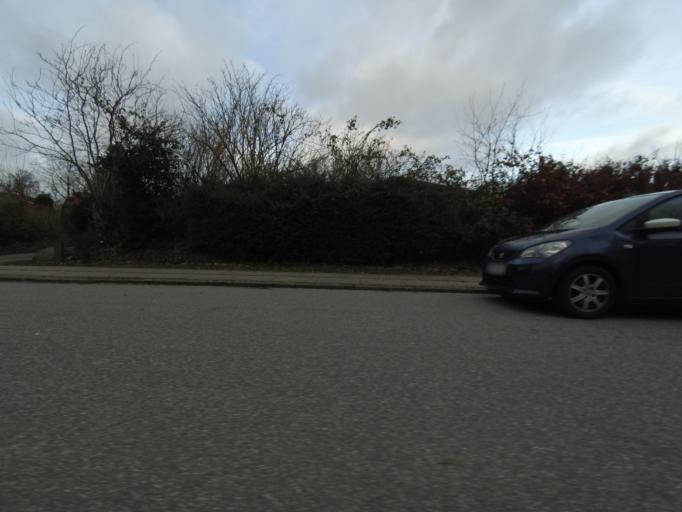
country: DK
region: Central Jutland
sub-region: Arhus Kommune
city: Arhus
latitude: 56.1231
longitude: 10.1825
